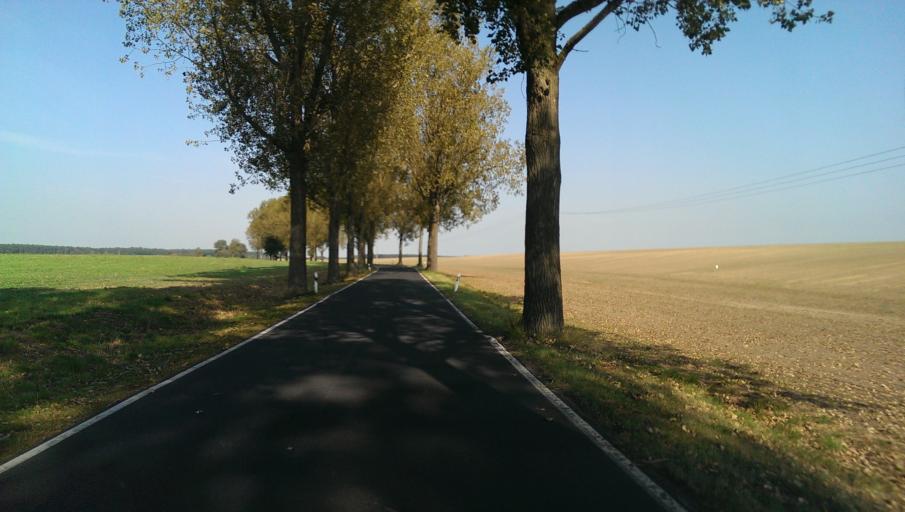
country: DE
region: Saxony-Anhalt
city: Kropstadt
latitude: 51.9711
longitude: 12.7352
